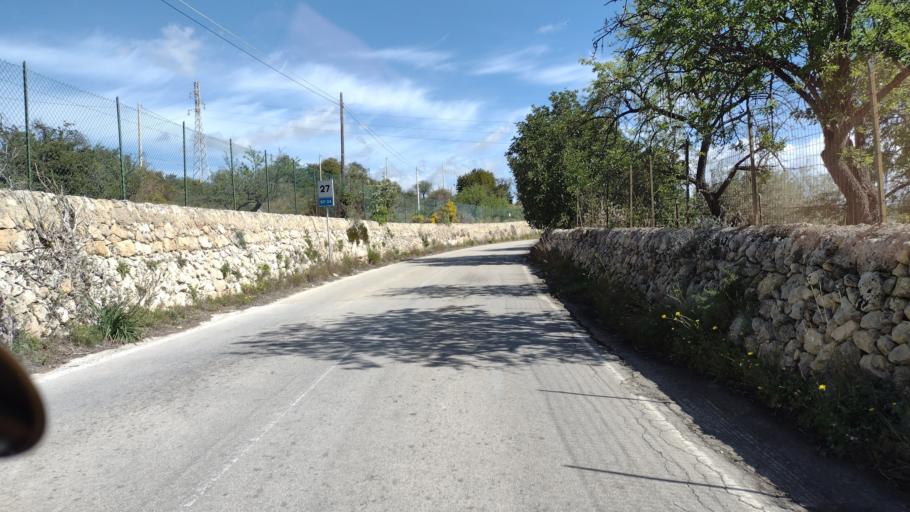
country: IT
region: Sicily
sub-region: Provincia di Siracusa
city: Noto
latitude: 36.8976
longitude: 15.0408
